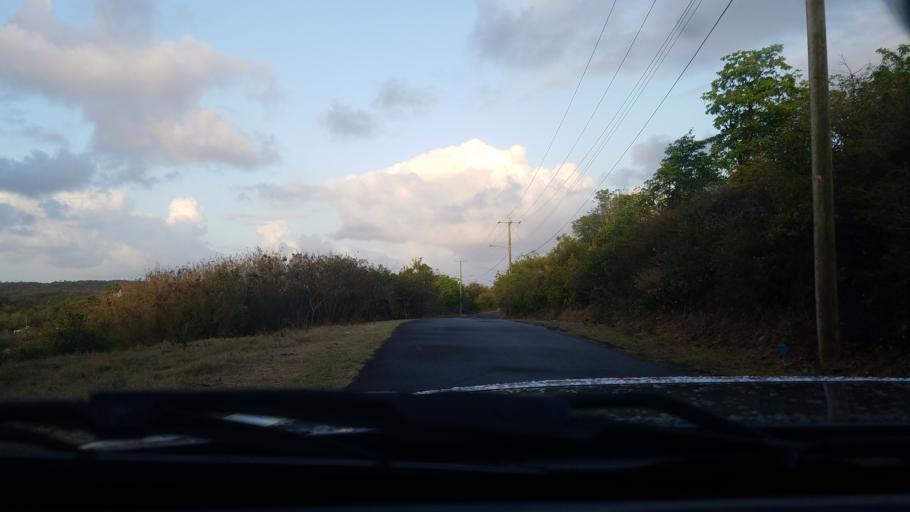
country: LC
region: Gros-Islet
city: Gros Islet
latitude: 14.0905
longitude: -60.9379
